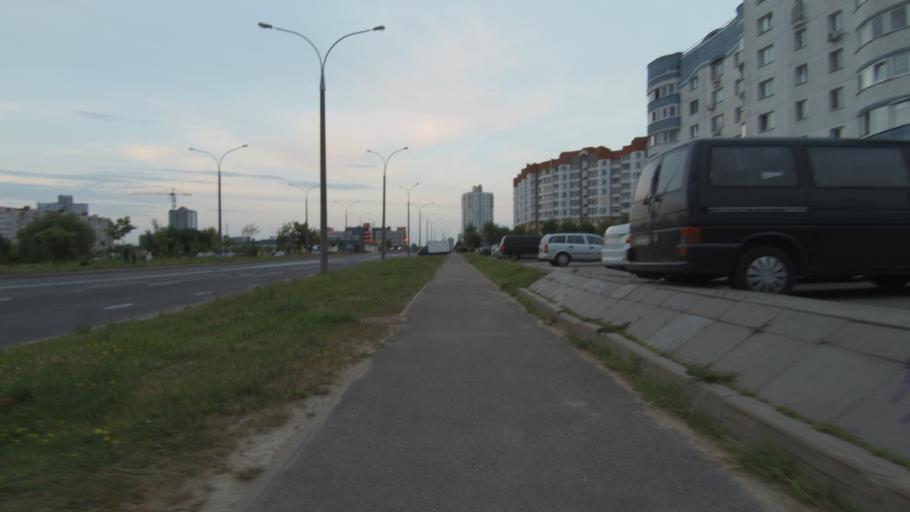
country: BY
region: Minsk
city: Syenitsa
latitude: 53.8391
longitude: 27.5651
